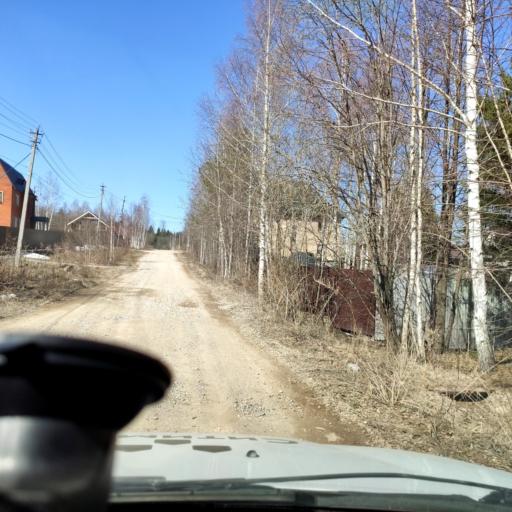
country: RU
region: Perm
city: Ferma
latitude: 57.9292
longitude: 56.4202
